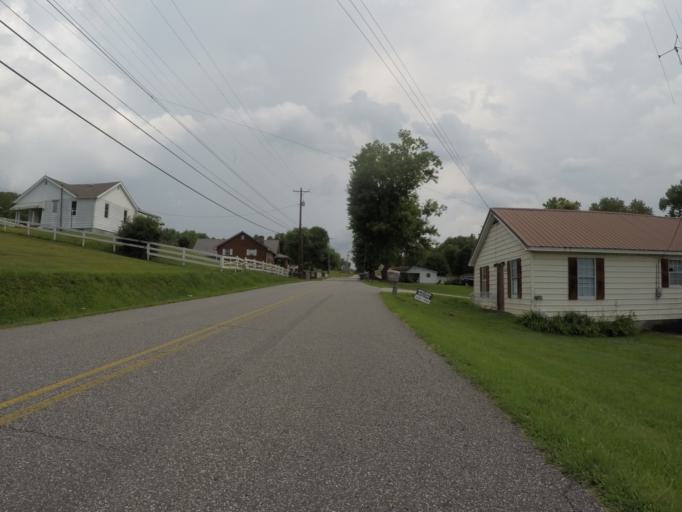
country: US
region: Kentucky
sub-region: Boyd County
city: Meads
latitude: 38.4329
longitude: -82.7088
